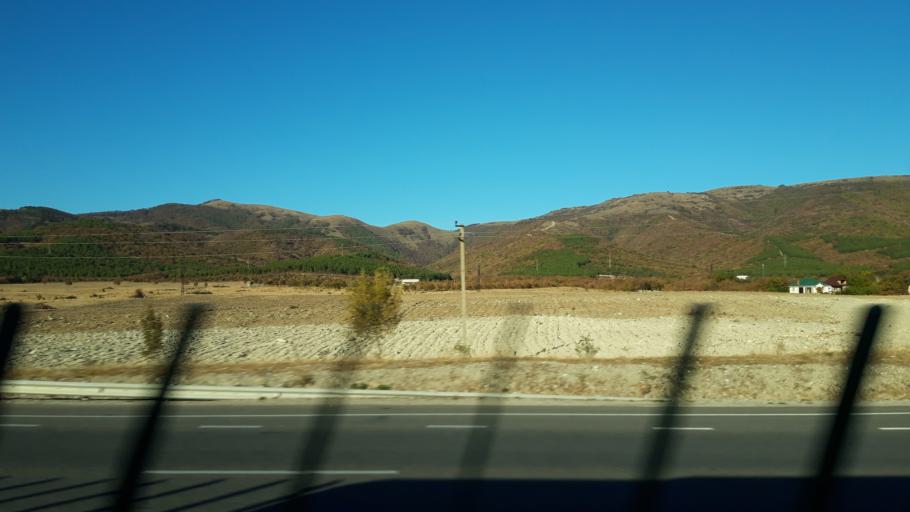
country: RU
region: Krasnodarskiy
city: Kabardinka
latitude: 44.6355
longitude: 37.9940
